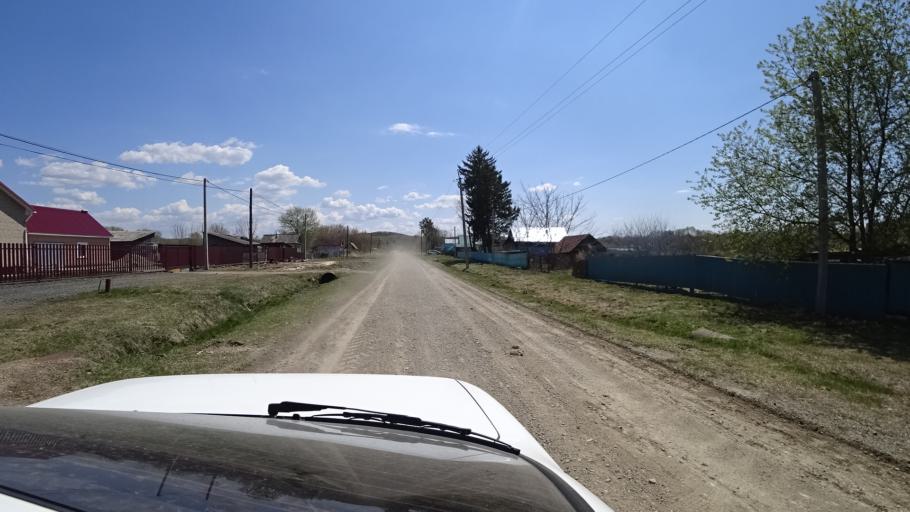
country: RU
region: Primorskiy
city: Lazo
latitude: 45.7925
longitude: 133.7640
